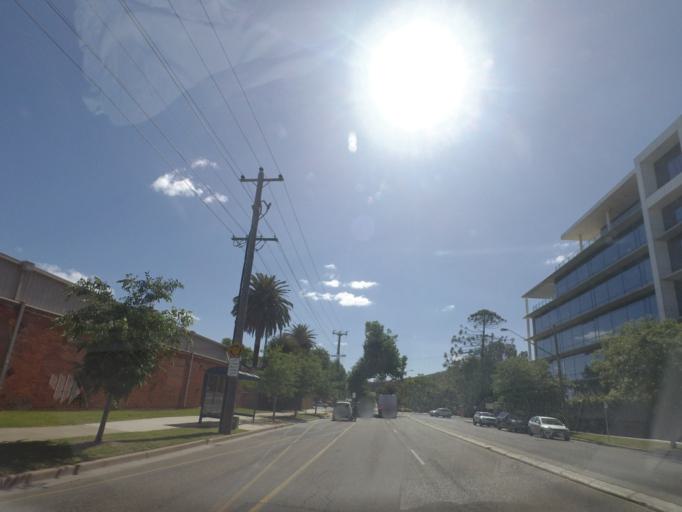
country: AU
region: New South Wales
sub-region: Albury Municipality
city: South Albury
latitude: -36.0823
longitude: 146.9111
